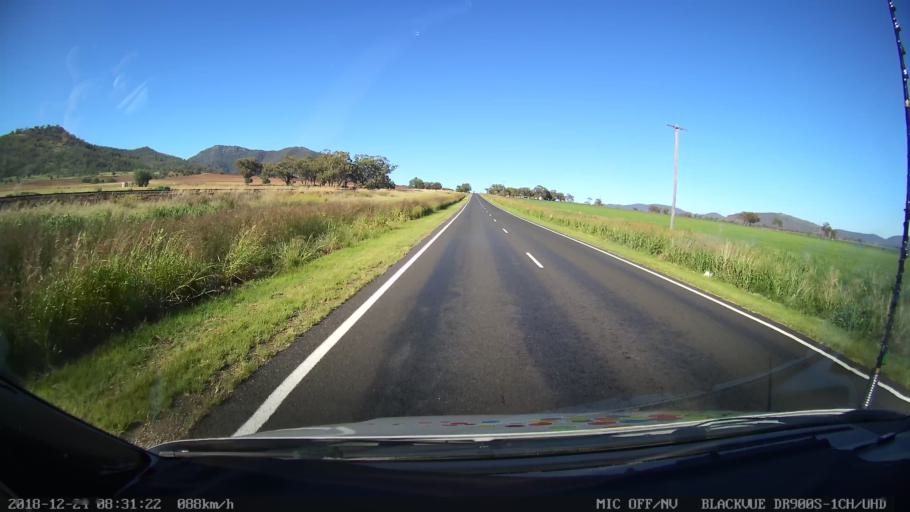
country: AU
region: New South Wales
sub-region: Tamworth Municipality
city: Phillip
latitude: -31.2731
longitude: 150.7126
